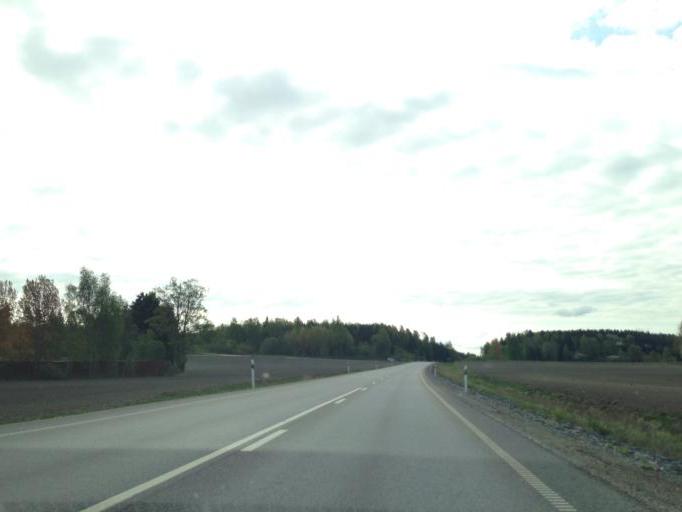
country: SE
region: Soedermanland
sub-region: Flens Kommun
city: Malmkoping
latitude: 59.1227
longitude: 16.7474
